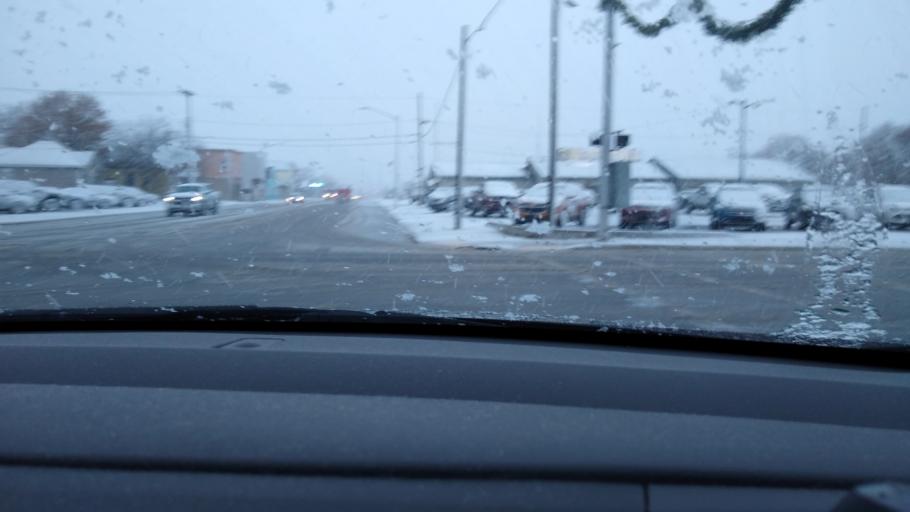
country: US
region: Michigan
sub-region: Delta County
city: Escanaba
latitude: 45.7494
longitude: -87.0717
